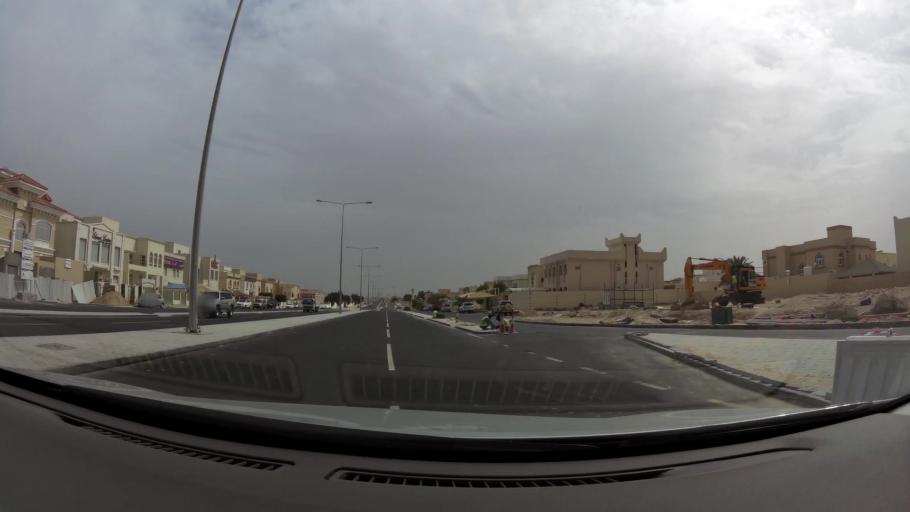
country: QA
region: Baladiyat ar Rayyan
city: Ar Rayyan
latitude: 25.3538
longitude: 51.4652
